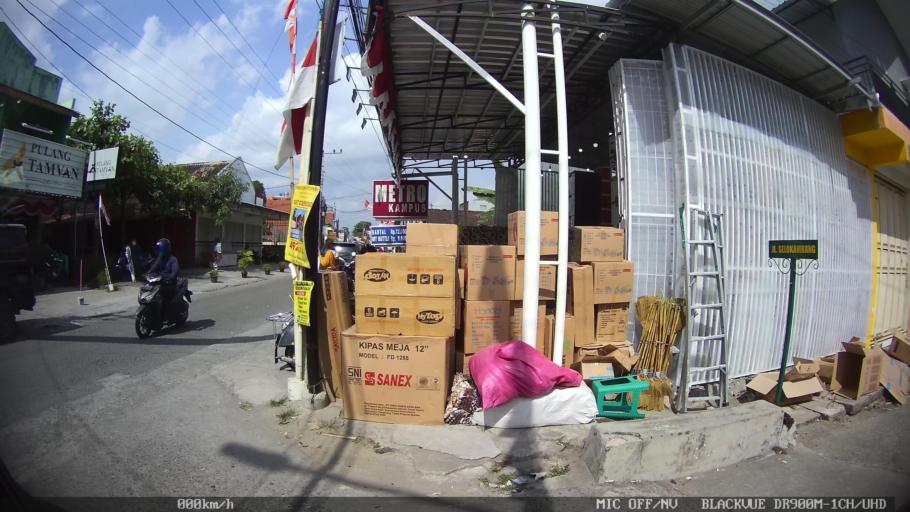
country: ID
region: Daerah Istimewa Yogyakarta
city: Kasihan
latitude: -7.8153
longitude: 110.3259
